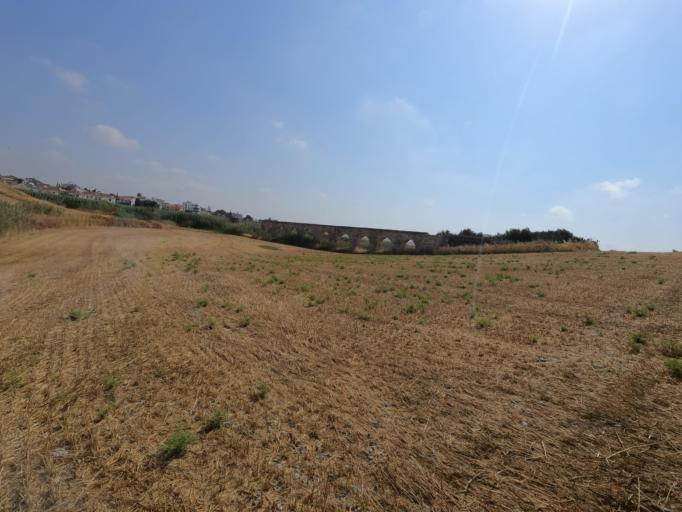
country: CY
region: Larnaka
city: Dhromolaxia
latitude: 34.9011
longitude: 33.5885
